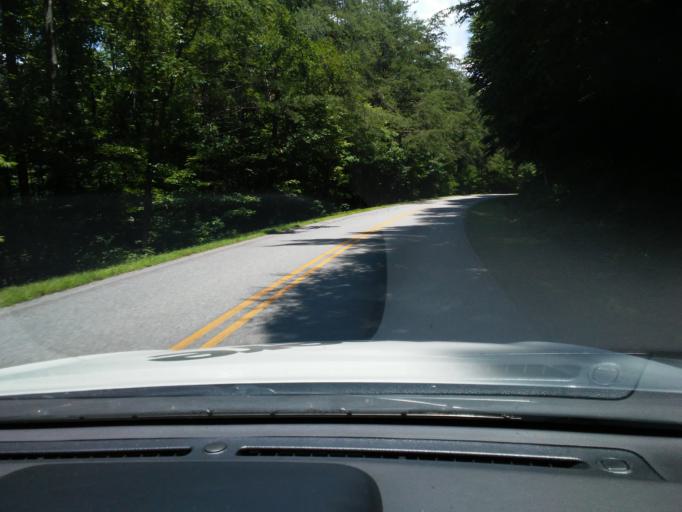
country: US
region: Georgia
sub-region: Towns County
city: Hiawassee
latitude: 34.8679
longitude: -83.7473
